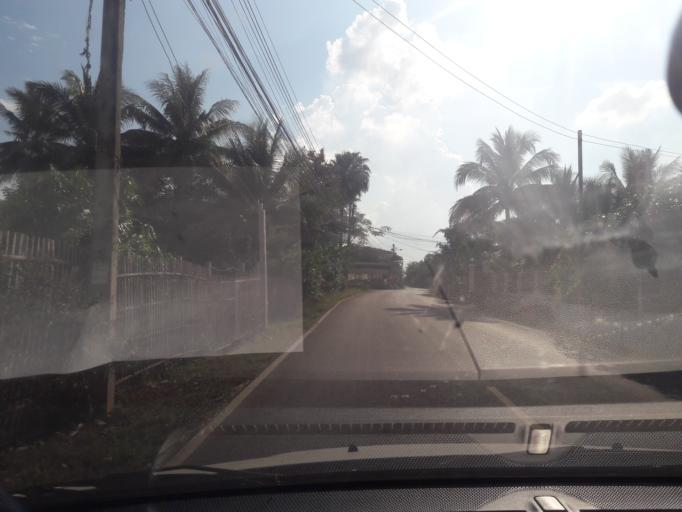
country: TH
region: Chiang Mai
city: San Kamphaeng
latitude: 18.7544
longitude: 99.1407
